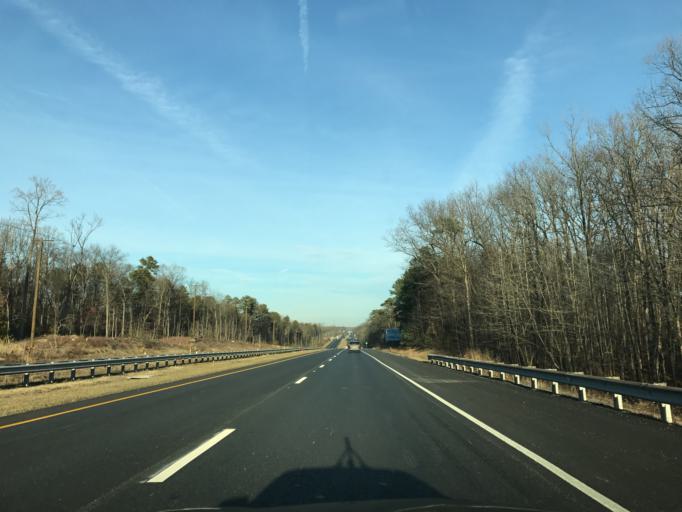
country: US
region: Maryland
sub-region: Cecil County
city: Charlestown
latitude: 39.5897
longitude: -75.9978
